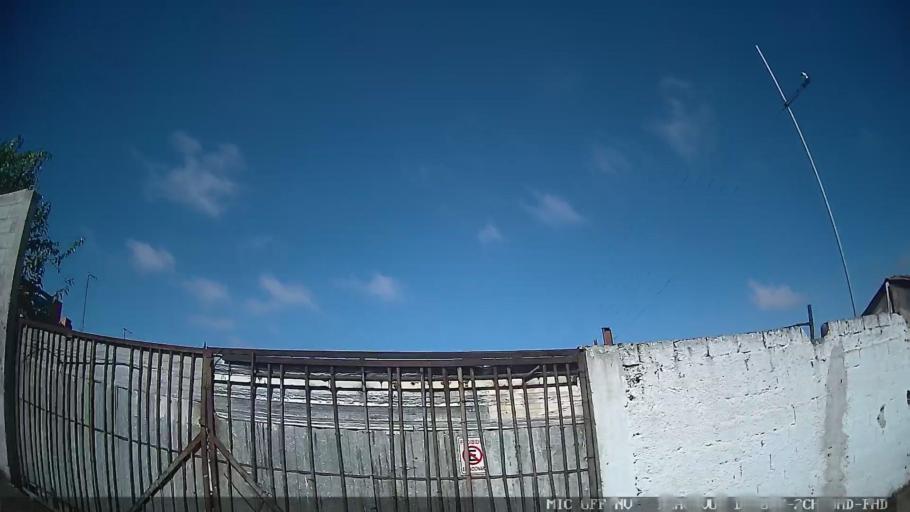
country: BR
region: Sao Paulo
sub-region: Itaquaquecetuba
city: Itaquaquecetuba
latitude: -23.4940
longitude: -46.3408
